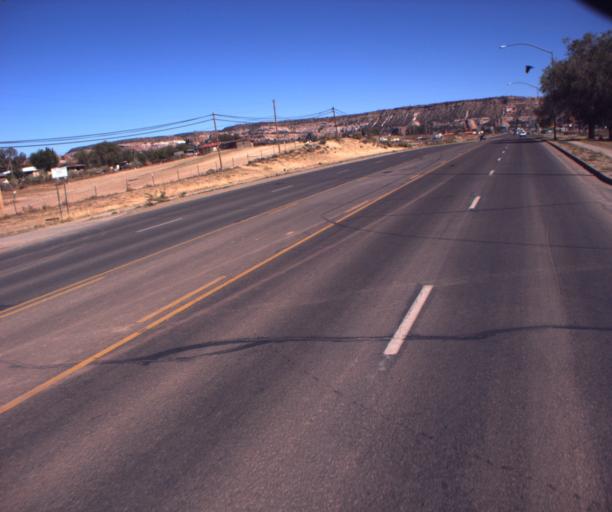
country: US
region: Arizona
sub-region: Apache County
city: Window Rock
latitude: 35.6615
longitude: -109.0673
